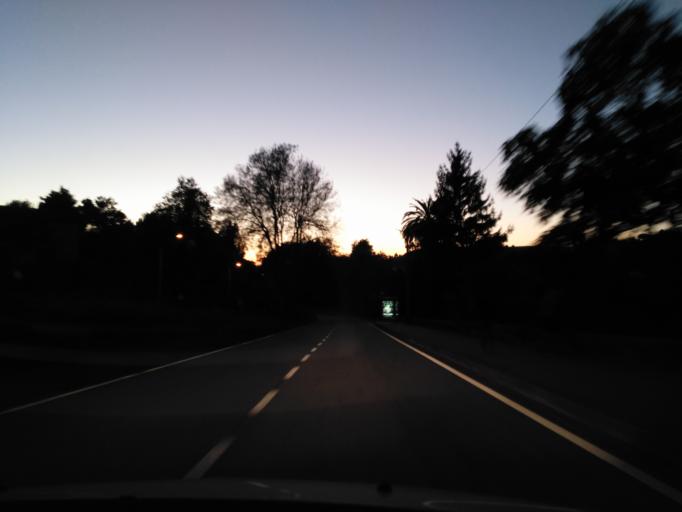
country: PT
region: Braga
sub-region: Braga
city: Braga
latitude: 41.5576
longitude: -8.3906
